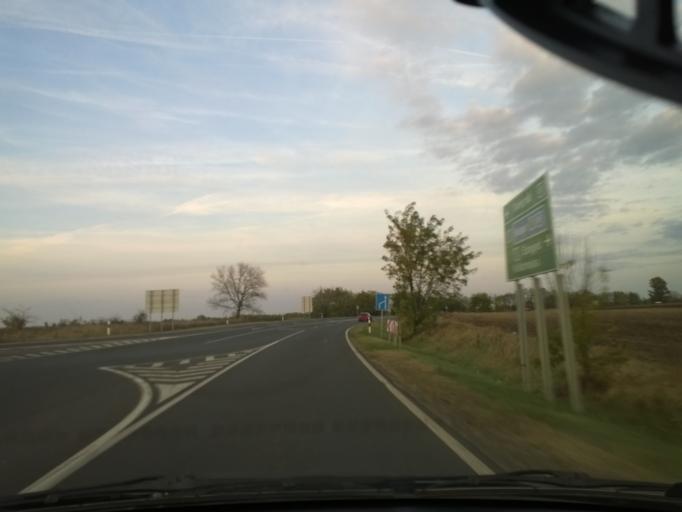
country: HU
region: Bacs-Kiskun
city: Kiskunfelegyhaza
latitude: 46.7055
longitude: 19.8900
